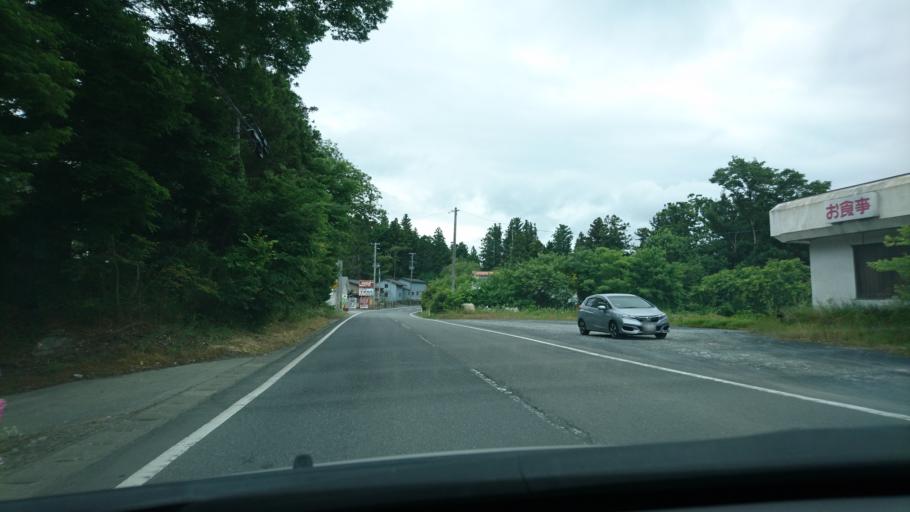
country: JP
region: Iwate
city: Ichinoseki
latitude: 38.7534
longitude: 141.2548
